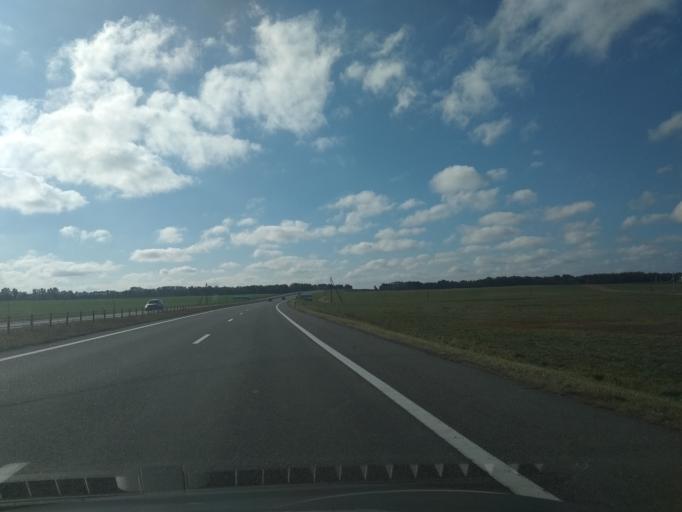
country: BY
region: Minsk
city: Stan'kava
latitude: 53.6909
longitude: 27.2080
